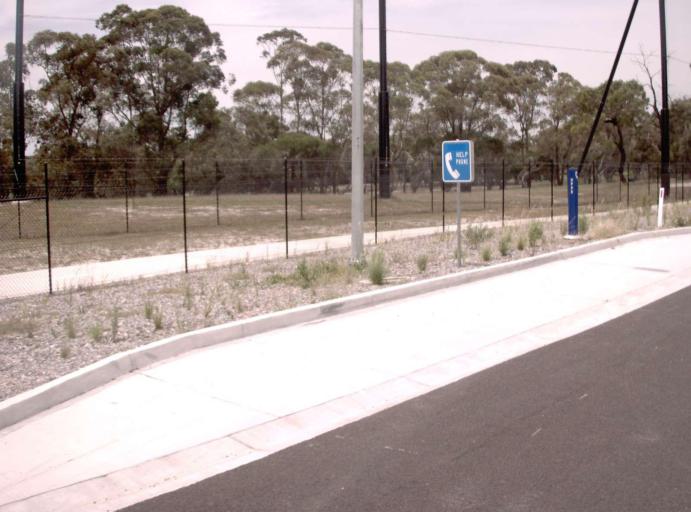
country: AU
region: Victoria
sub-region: Frankston
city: Frankston North
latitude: -38.1301
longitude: 145.1730
